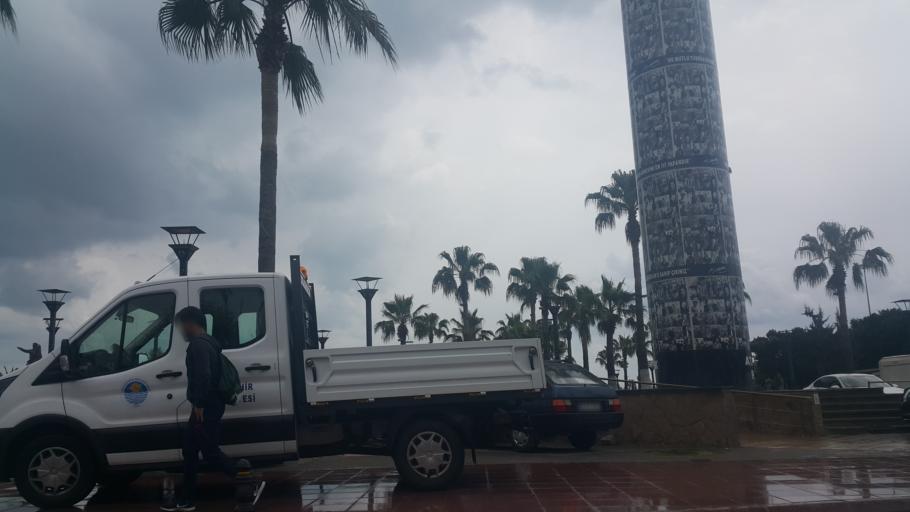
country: TR
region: Mersin
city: Mercin
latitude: 36.7923
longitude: 34.6257
